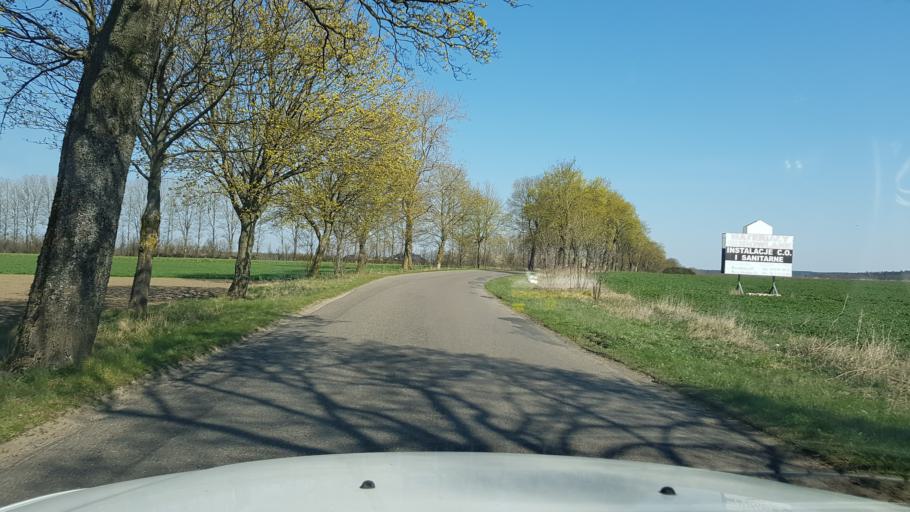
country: PL
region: West Pomeranian Voivodeship
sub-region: Powiat slawienski
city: Slawno
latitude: 54.3781
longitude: 16.6867
